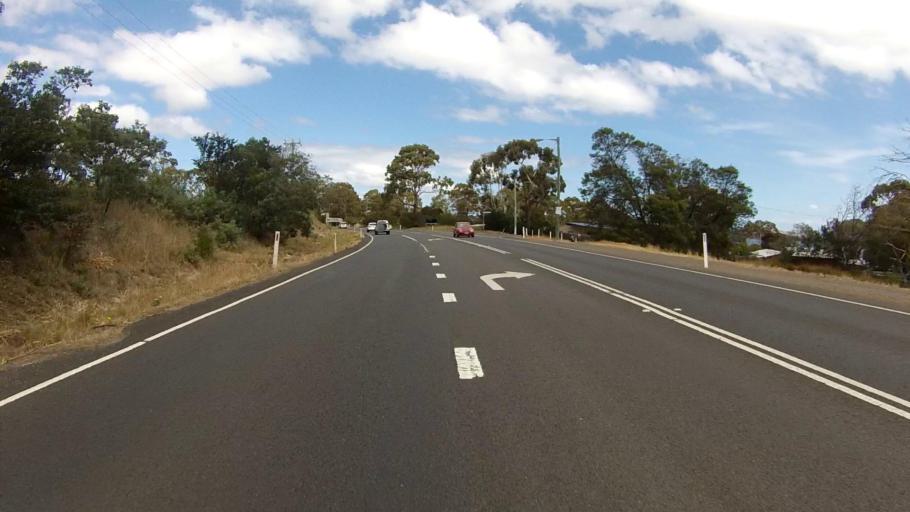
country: AU
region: Tasmania
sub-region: Sorell
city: Sorell
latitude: -42.8400
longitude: 147.6225
